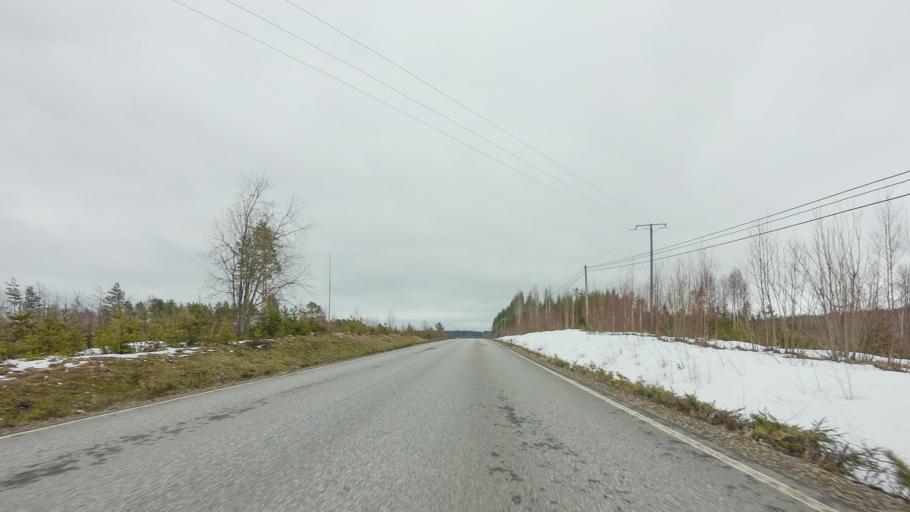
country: FI
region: Southern Savonia
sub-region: Savonlinna
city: Savonlinna
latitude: 61.9555
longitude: 28.8463
